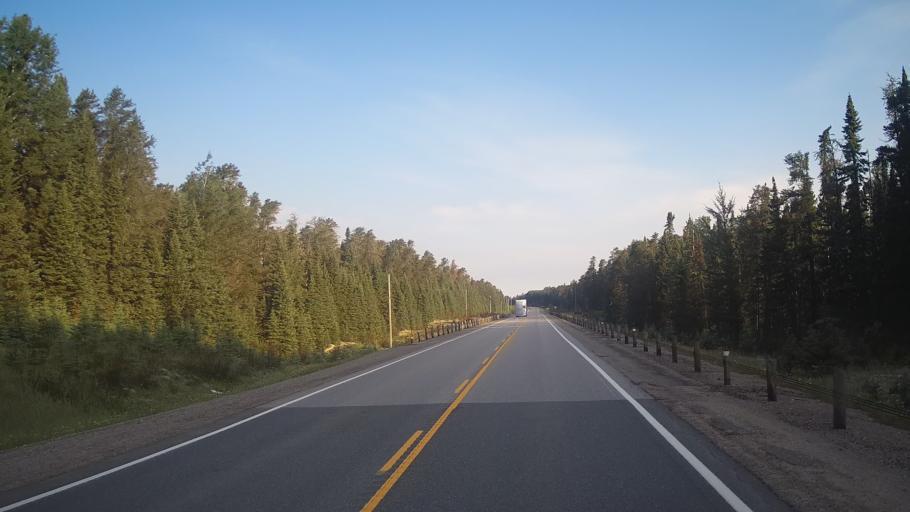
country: CA
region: Ontario
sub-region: Rainy River District
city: Atikokan
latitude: 49.3543
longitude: -91.5266
